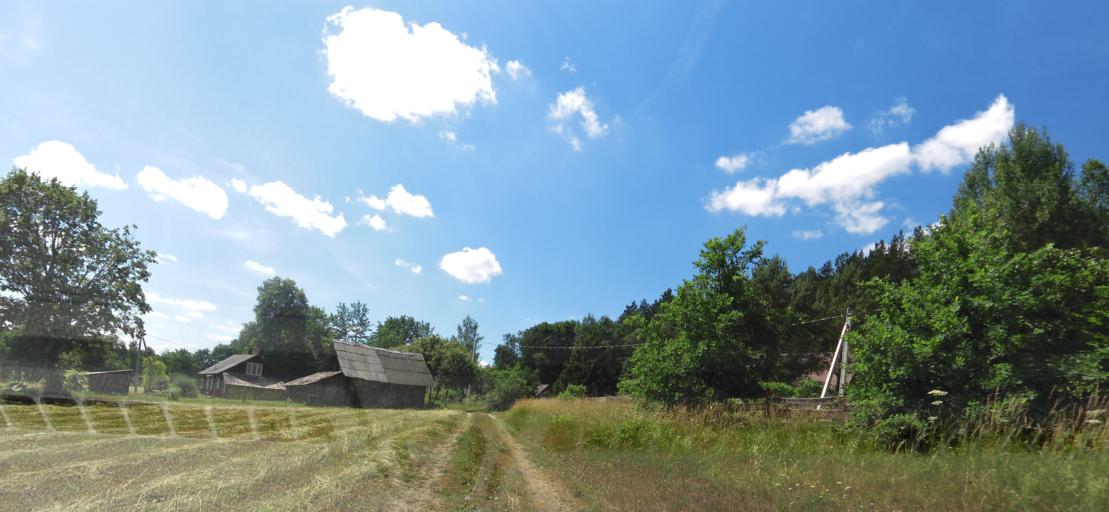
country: LT
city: Nemencine
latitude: 54.8724
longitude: 25.5738
